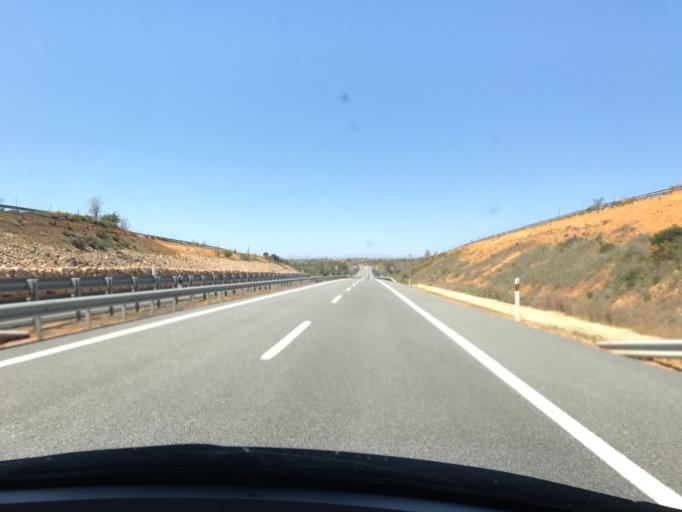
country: ES
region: Castille and Leon
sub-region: Provincia de Leon
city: Valverde de la Virgen
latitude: 42.5643
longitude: -5.6672
